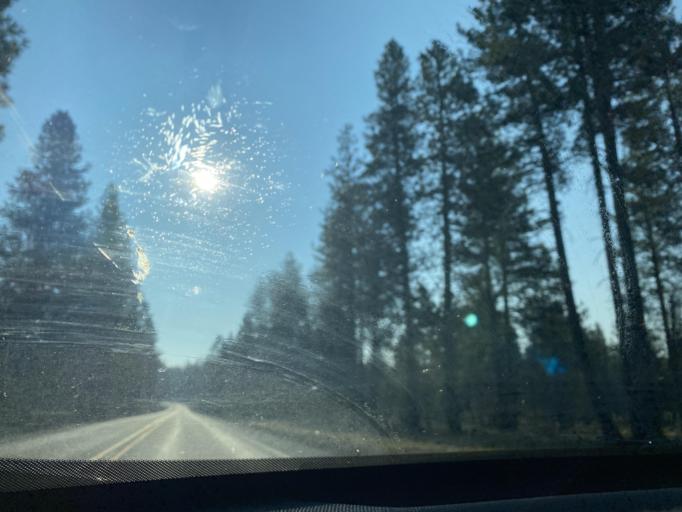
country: US
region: Oregon
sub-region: Deschutes County
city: Sunriver
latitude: 43.8694
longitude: -121.4187
